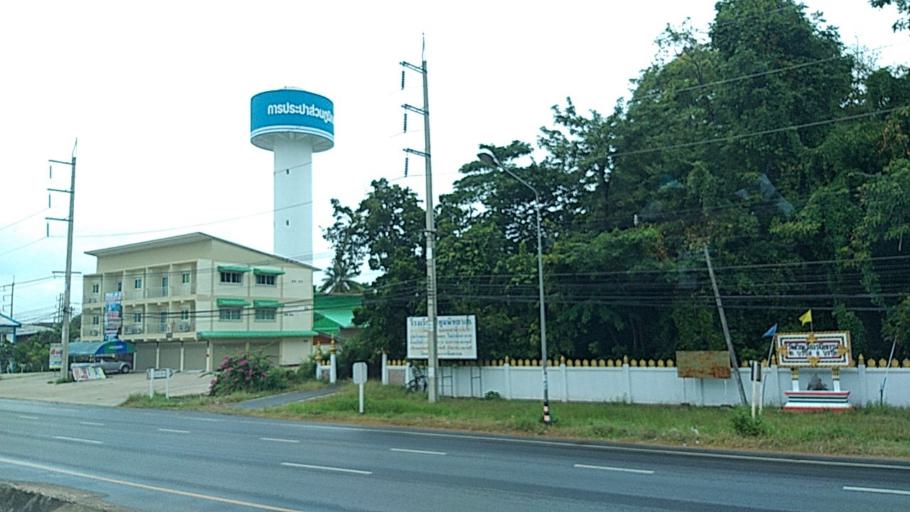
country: TH
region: Maha Sarakham
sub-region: Amphoe Borabue
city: Borabue
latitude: 16.0461
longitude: 103.1250
